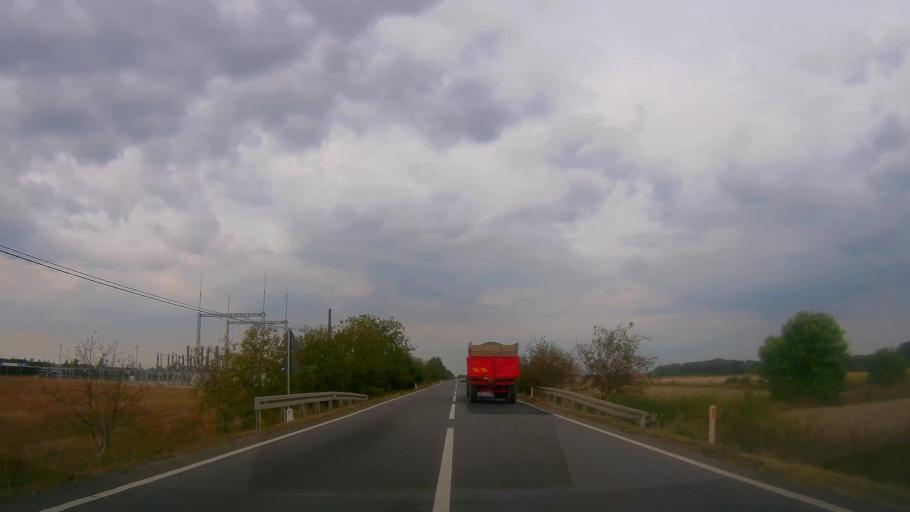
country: RO
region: Satu Mare
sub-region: Comuna Turulung
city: Draguseni
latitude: 47.8763
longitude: 23.0540
